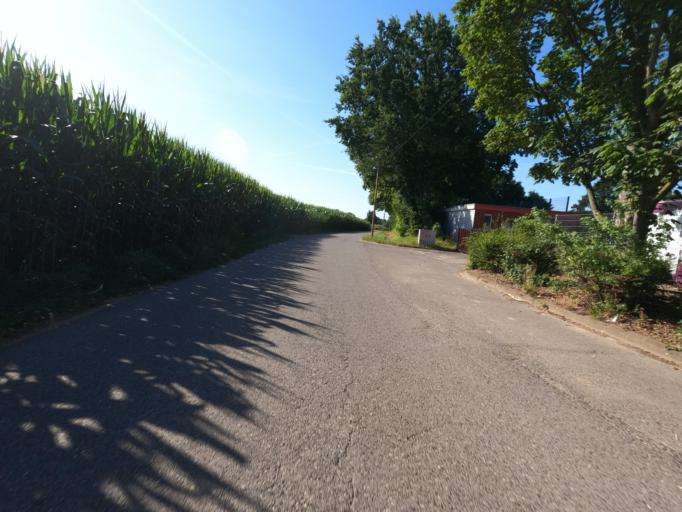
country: DE
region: North Rhine-Westphalia
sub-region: Regierungsbezirk Koln
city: Heinsberg
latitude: 51.0798
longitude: 6.1276
